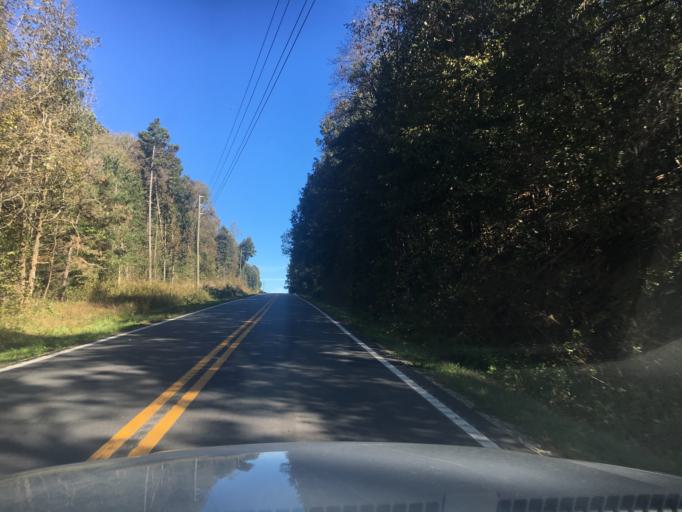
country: US
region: North Carolina
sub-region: Burke County
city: Glen Alpine
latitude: 35.6075
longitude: -81.8155
